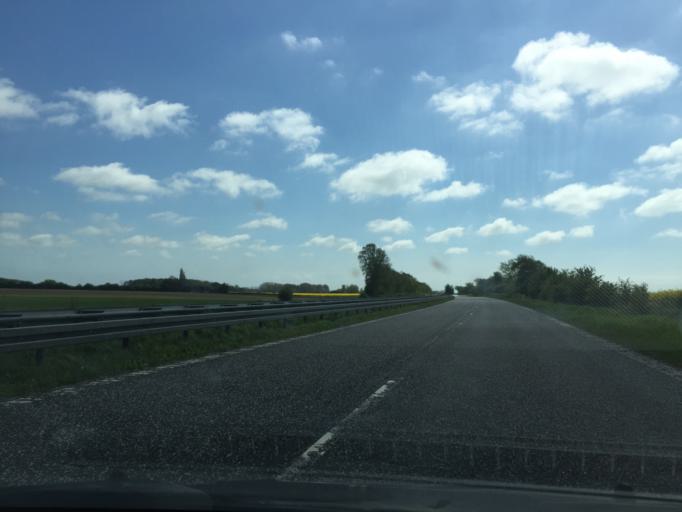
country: DK
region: Zealand
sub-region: Lolland Kommune
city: Holeby
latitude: 54.7377
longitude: 11.4422
